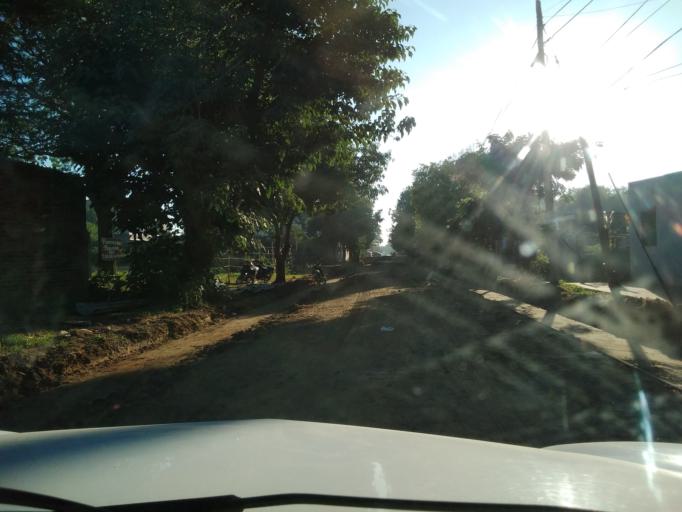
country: AR
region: Corrientes
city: Corrientes
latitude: -27.4790
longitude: -58.7882
